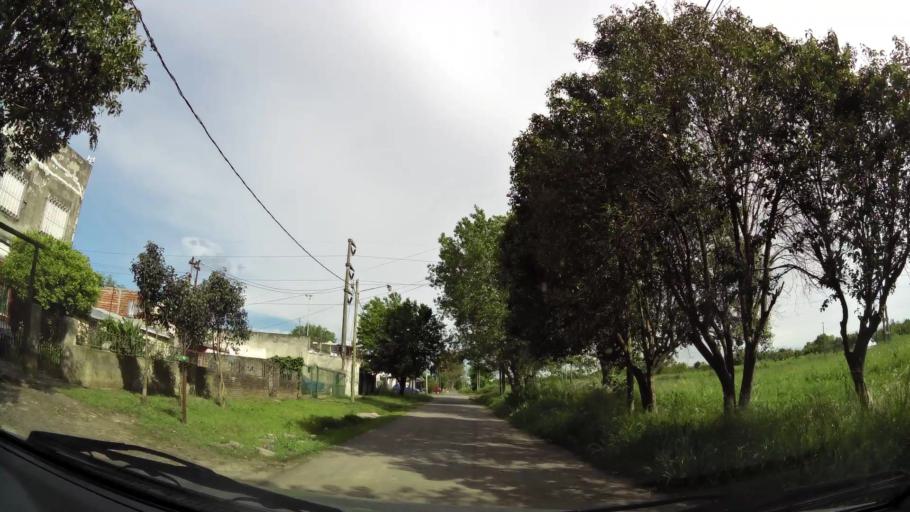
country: AR
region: Buenos Aires
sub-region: Partido de Almirante Brown
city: Adrogue
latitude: -34.8127
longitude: -58.3515
